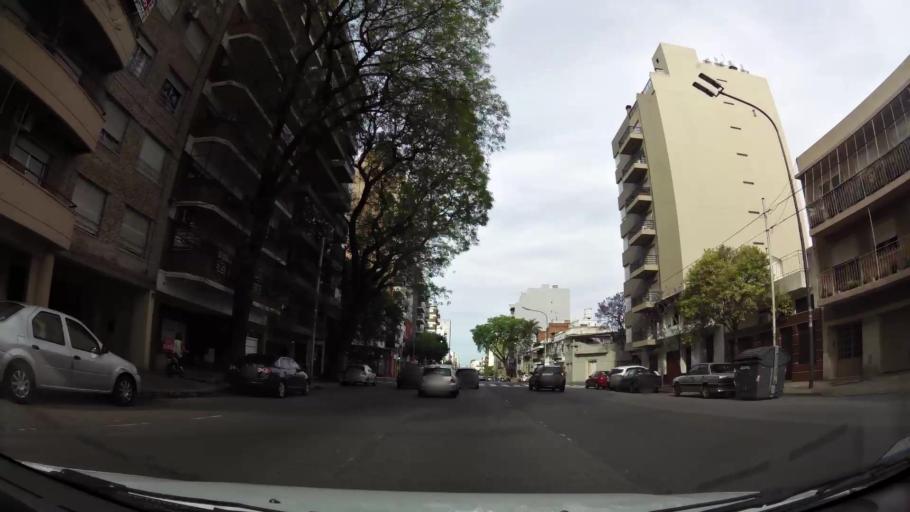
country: AR
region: Buenos Aires F.D.
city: Villa Santa Rita
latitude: -34.6371
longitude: -58.4728
